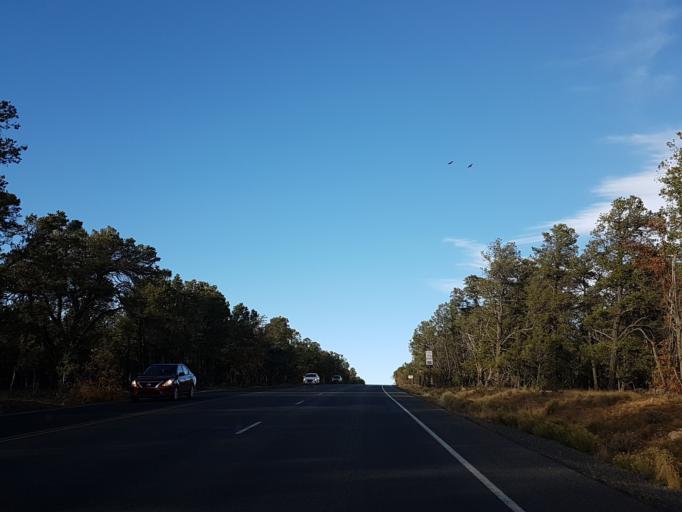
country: US
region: Arizona
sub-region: Coconino County
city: Grand Canyon Village
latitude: 35.9938
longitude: -112.1229
